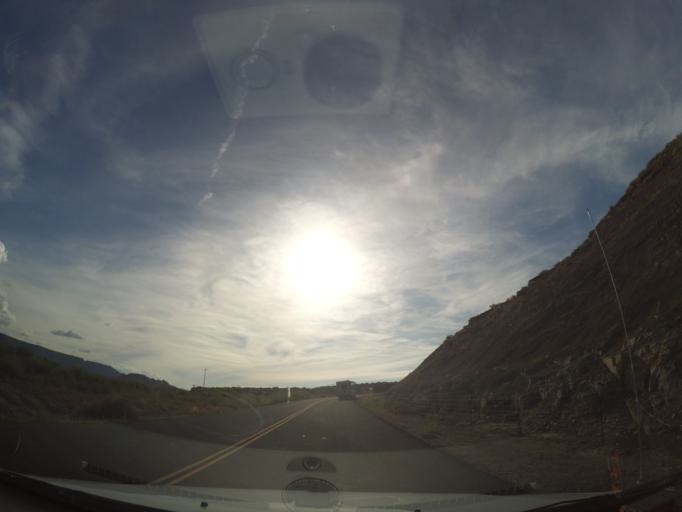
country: US
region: Utah
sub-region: Washington County
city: LaVerkin
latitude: 37.2052
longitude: -113.1728
